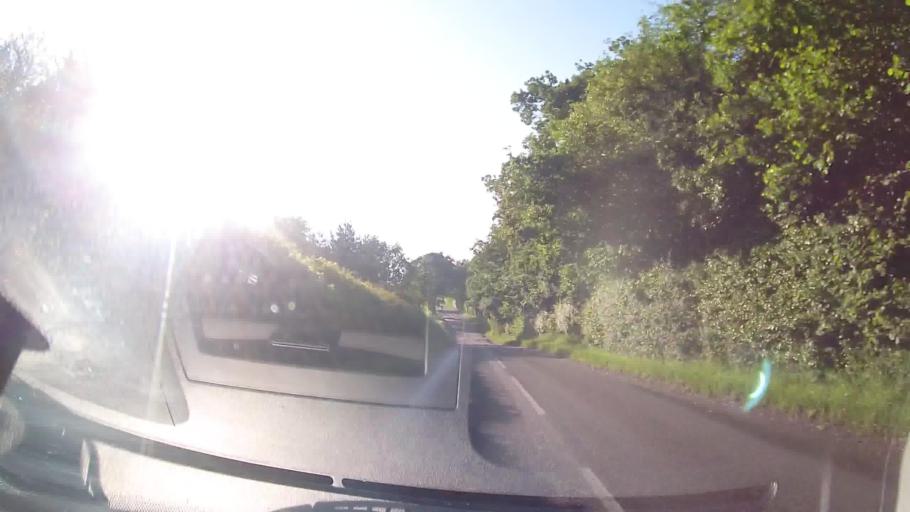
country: GB
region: England
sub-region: Leicestershire
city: Markfield
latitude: 52.6561
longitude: -1.2584
